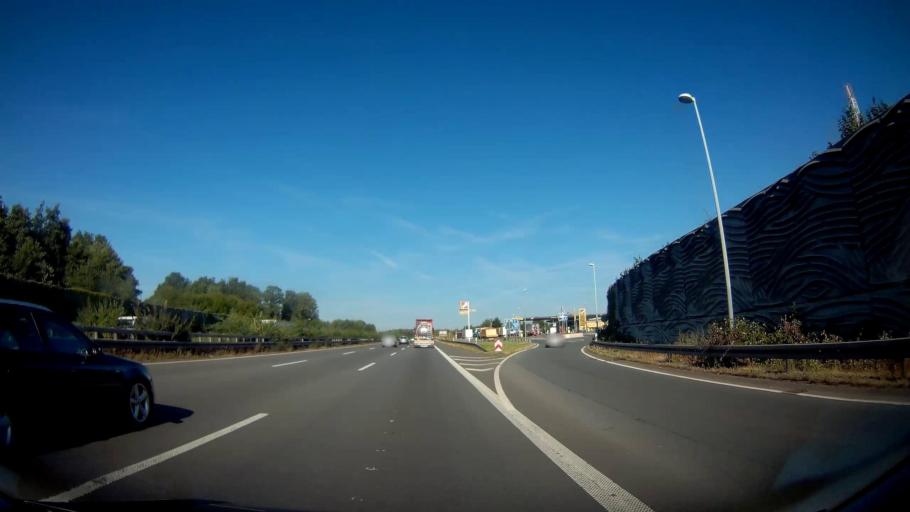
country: DE
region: North Rhine-Westphalia
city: Herten
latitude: 51.5700
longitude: 7.1057
